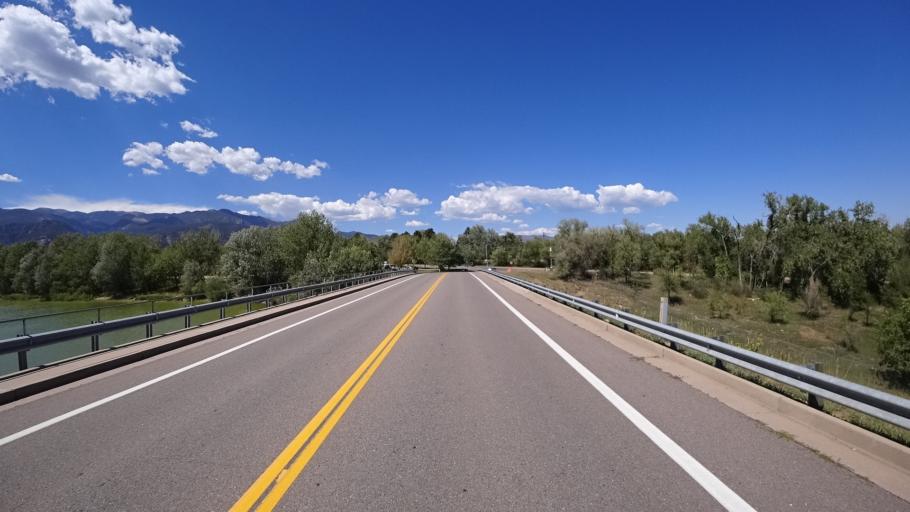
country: US
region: Colorado
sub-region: El Paso County
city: Colorado Springs
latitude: 38.7946
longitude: -104.8294
